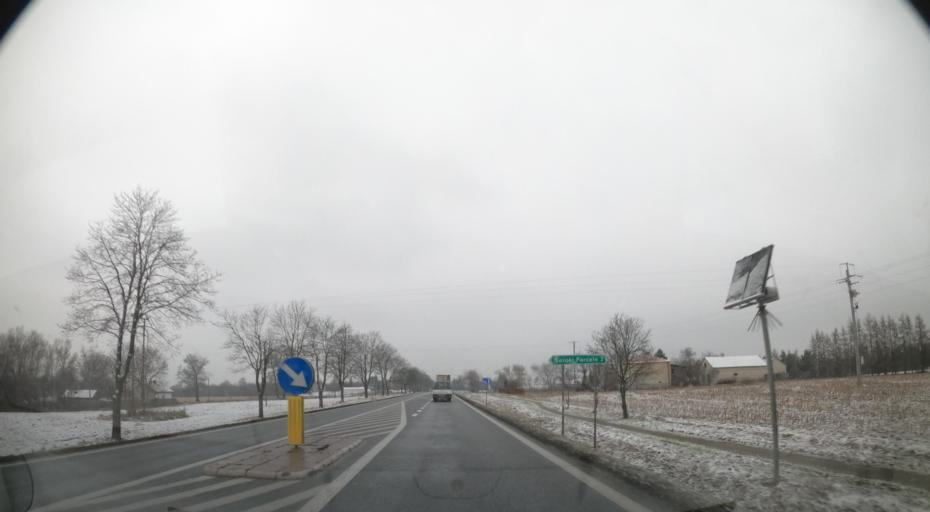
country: PL
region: Masovian Voivodeship
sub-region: Powiat sochaczewski
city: Paprotnia
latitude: 52.2086
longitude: 20.4664
